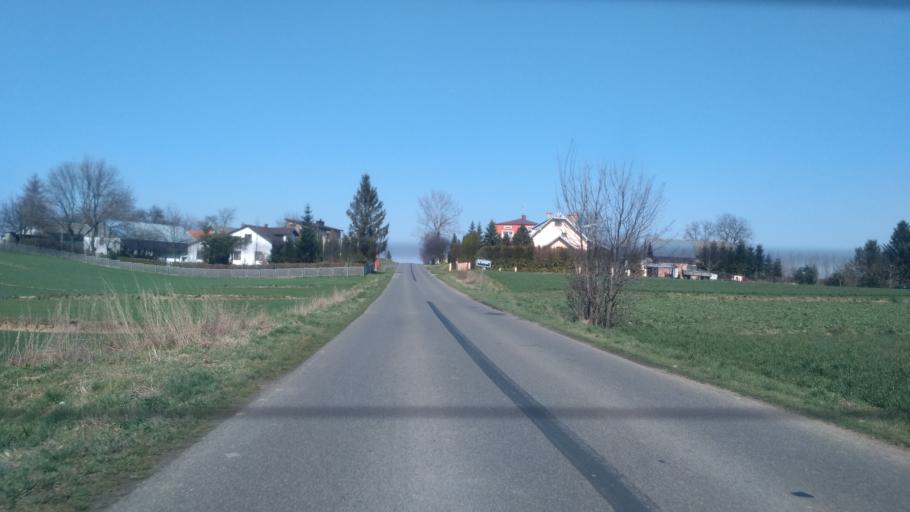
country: PL
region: Subcarpathian Voivodeship
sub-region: Powiat jaroslawski
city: Pawlosiow
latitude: 49.9531
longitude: 22.6657
